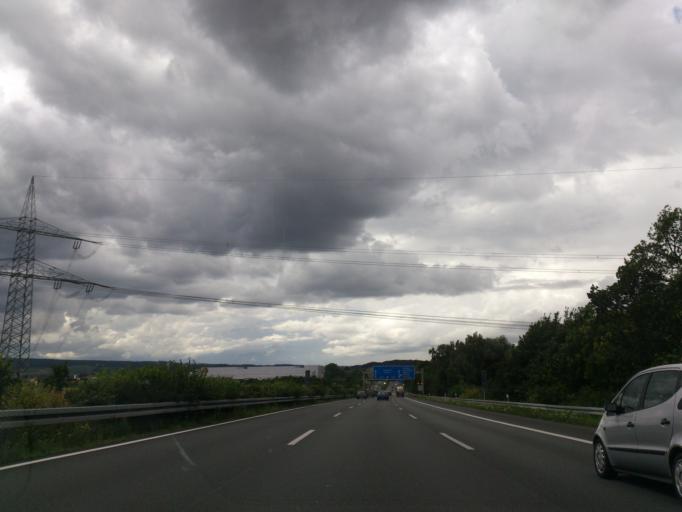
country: DE
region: Lower Saxony
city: Lauenau
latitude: 52.2883
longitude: 9.3572
